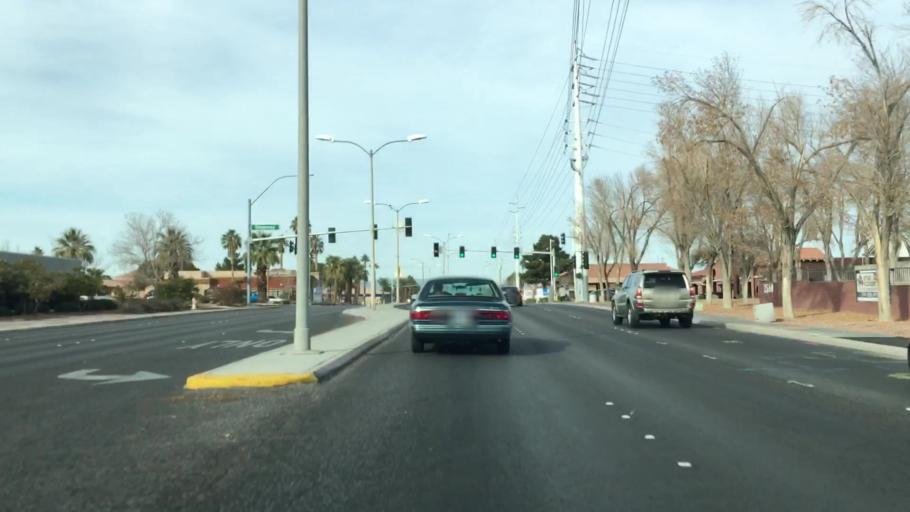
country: US
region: Nevada
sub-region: Clark County
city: Whitney
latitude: 36.0685
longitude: -115.0824
